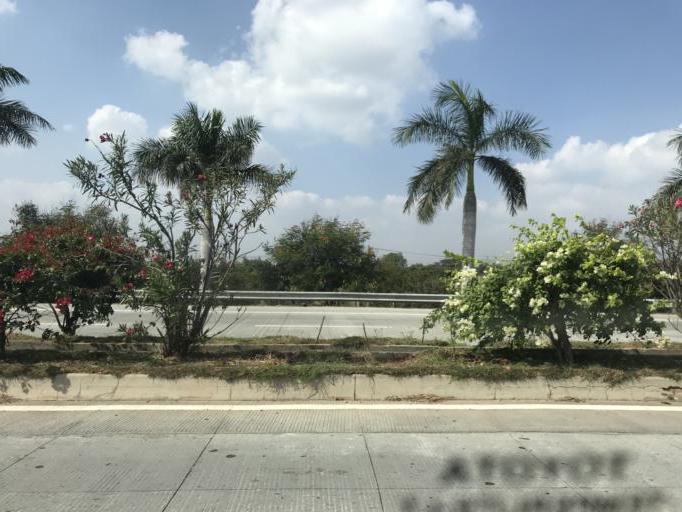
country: IN
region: Karnataka
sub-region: Bangalore Urban
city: Bangalore
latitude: 12.8845
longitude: 77.5024
